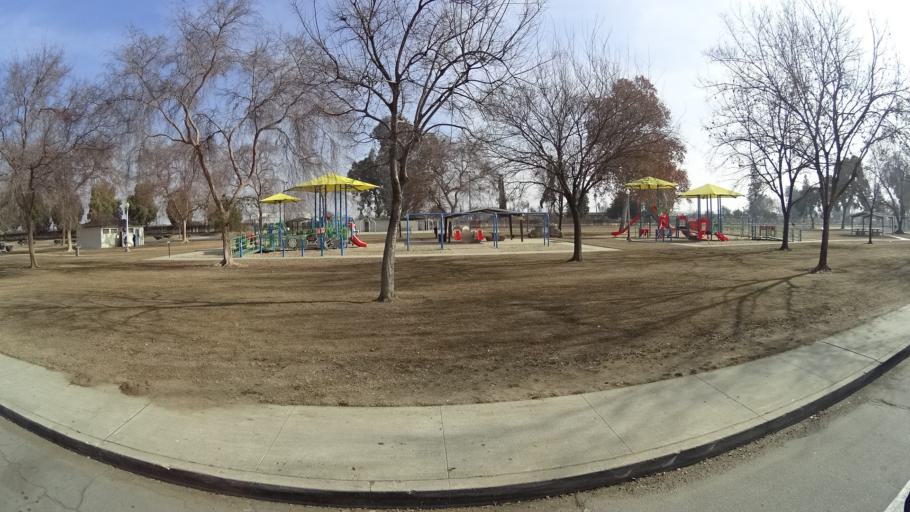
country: US
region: California
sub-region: Kern County
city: Bakersfield
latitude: 35.3420
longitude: -119.0158
